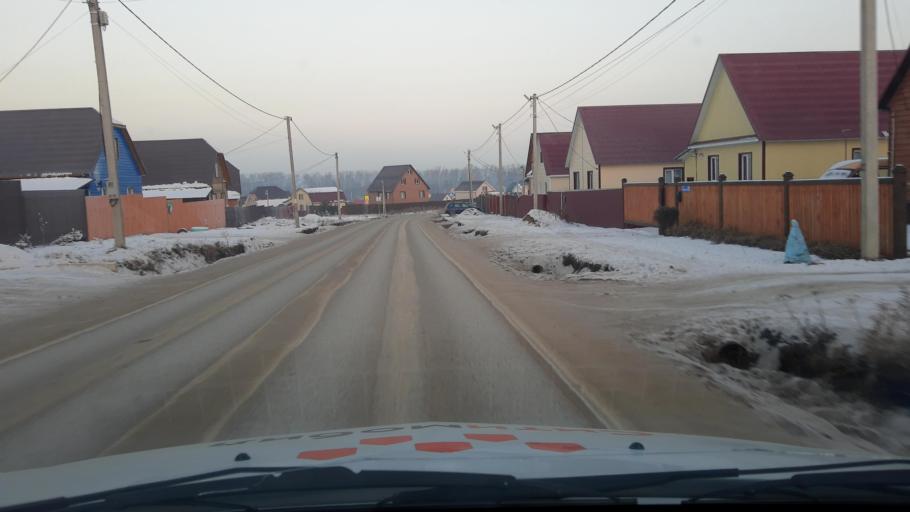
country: RU
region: Bashkortostan
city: Iglino
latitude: 54.8274
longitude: 56.4372
